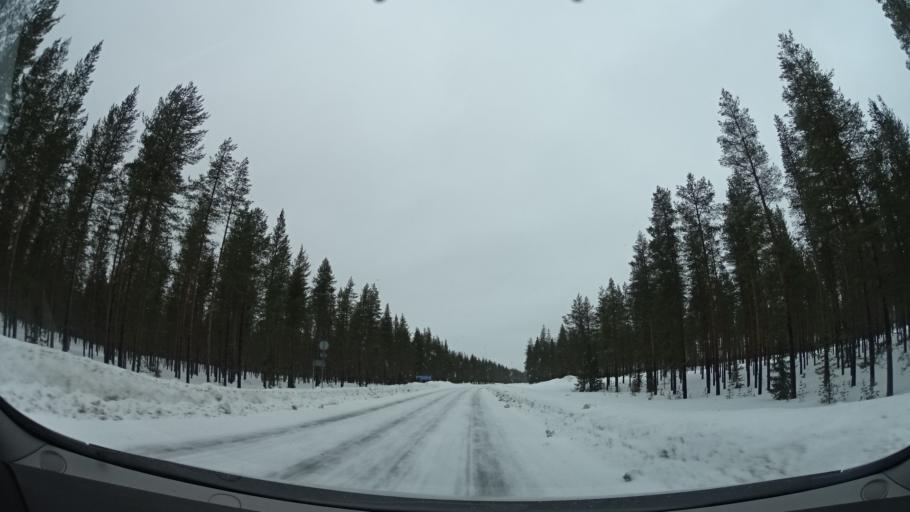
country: SE
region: Vaesterbotten
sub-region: Mala Kommun
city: Mala
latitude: 65.1243
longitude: 18.8729
